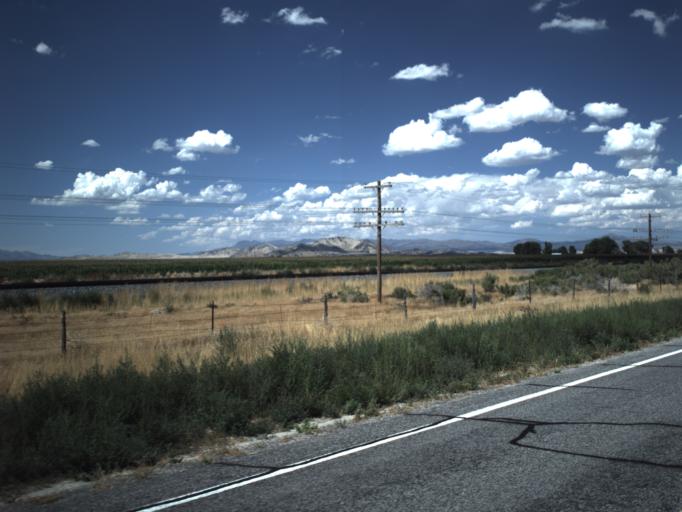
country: US
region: Utah
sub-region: Millard County
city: Delta
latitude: 39.5307
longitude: -112.3695
